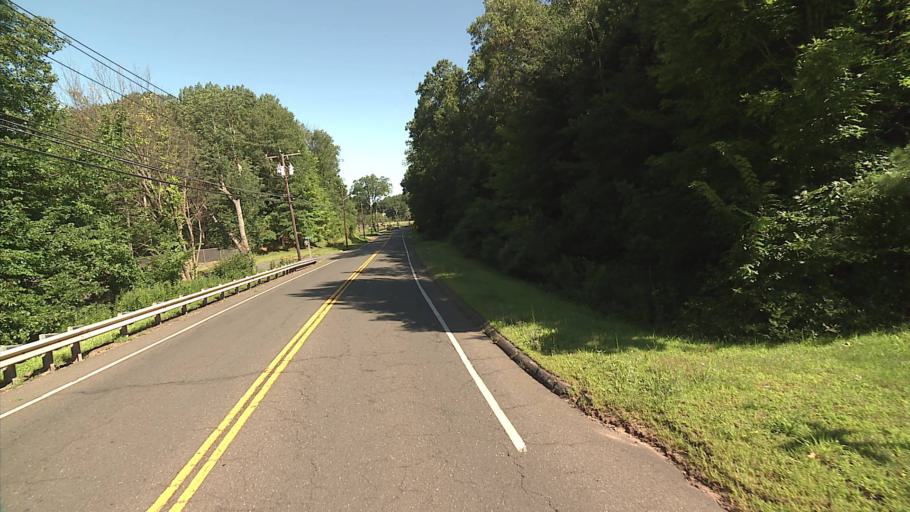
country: US
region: Connecticut
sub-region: Hartford County
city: Weatogue
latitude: 41.7981
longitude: -72.8182
